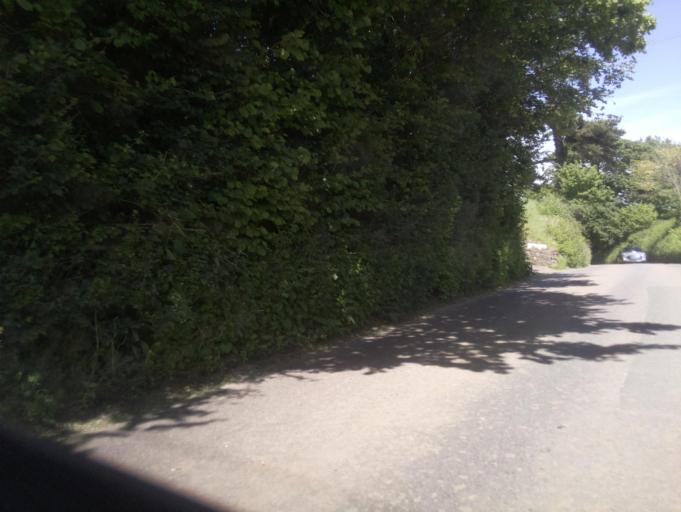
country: GB
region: England
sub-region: Devon
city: Ottery St Mary
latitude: 50.7394
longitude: -3.2730
